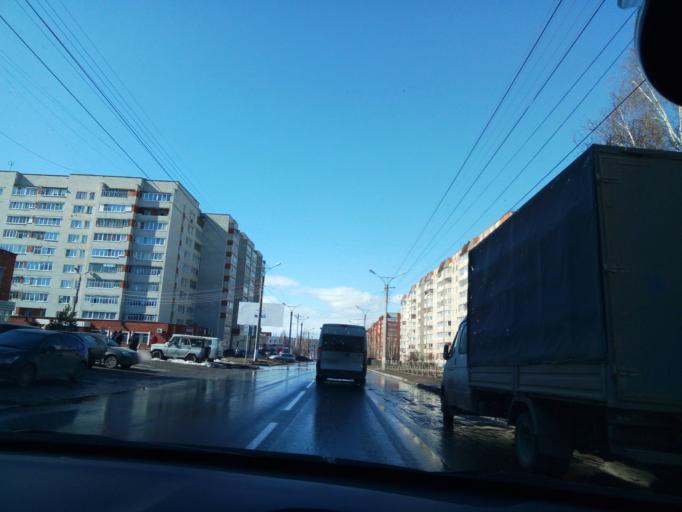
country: RU
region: Chuvashia
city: Novyye Lapsary
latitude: 56.1137
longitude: 47.1823
